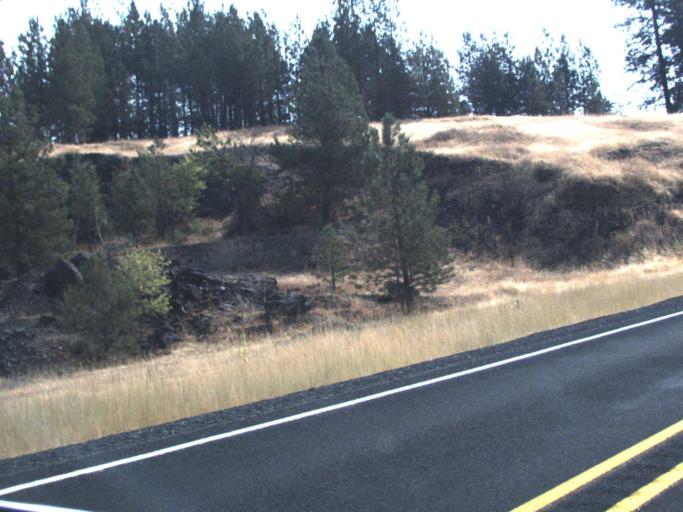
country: US
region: Idaho
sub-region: Latah County
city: Moscow
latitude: 46.9296
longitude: -117.0904
